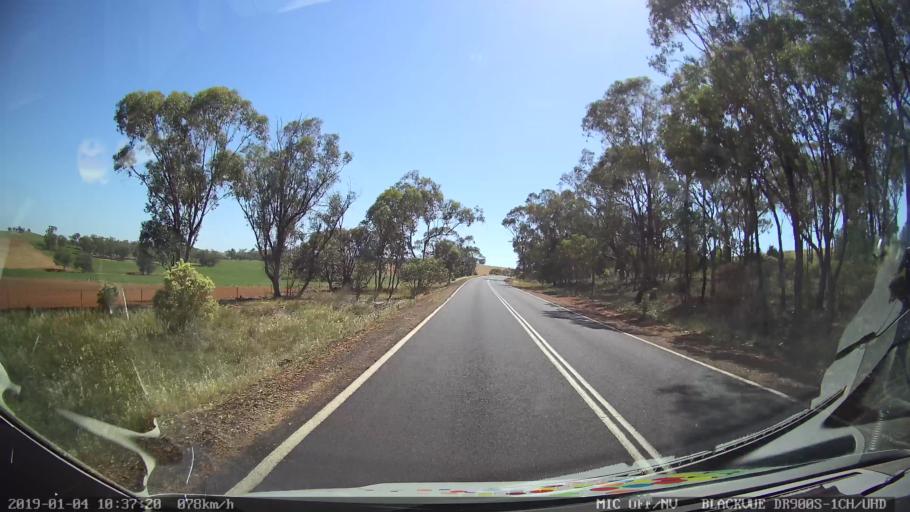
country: AU
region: New South Wales
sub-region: Cabonne
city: Canowindra
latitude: -33.2966
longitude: 148.6934
